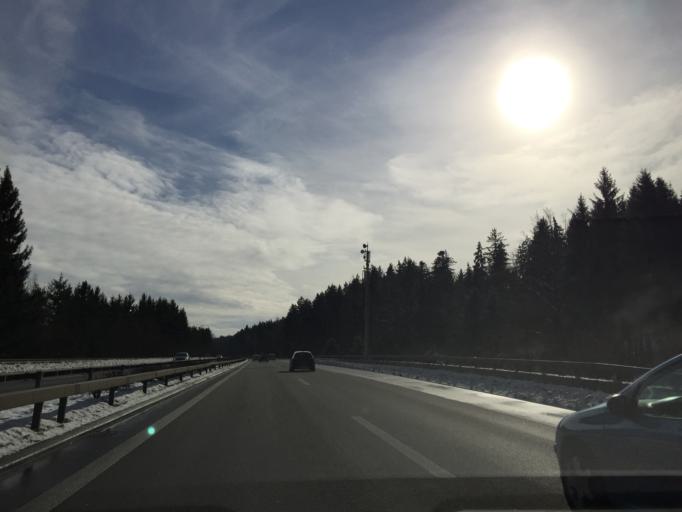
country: CH
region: Zurich
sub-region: Bezirk Horgen
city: Oberrieden / Berg
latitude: 47.2689
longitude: 8.5720
